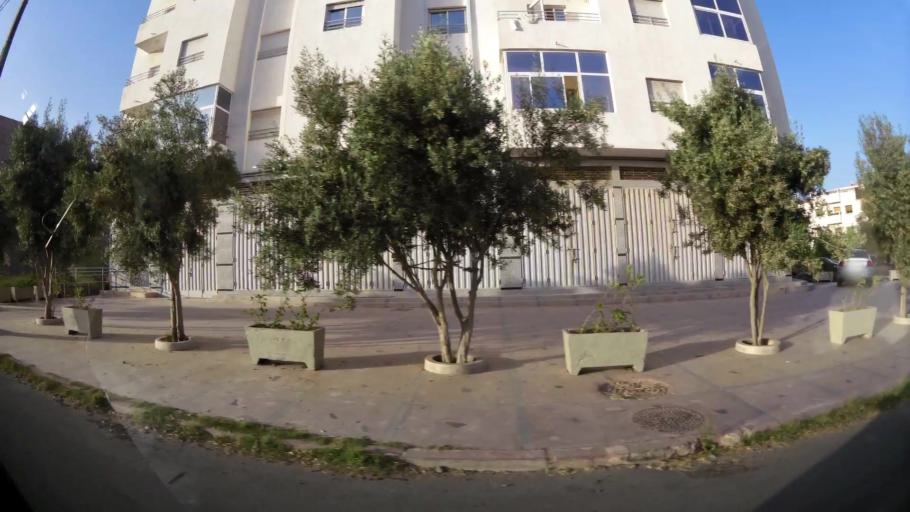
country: MA
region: Oued ed Dahab-Lagouira
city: Dakhla
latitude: 30.3930
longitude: -9.5432
